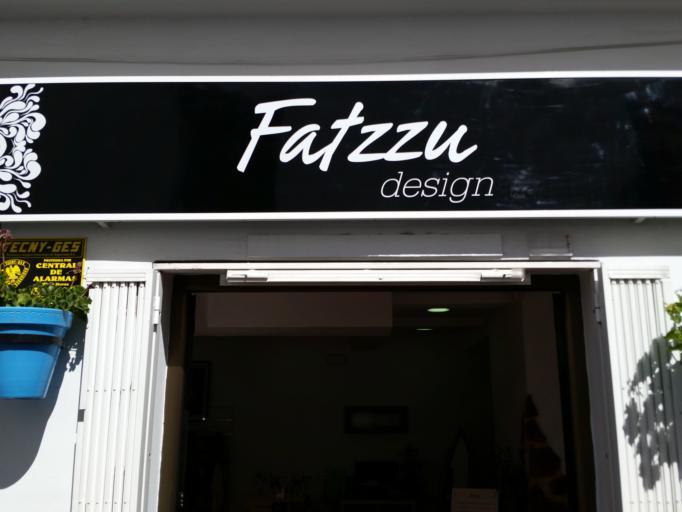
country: ES
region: Andalusia
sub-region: Provincia de Malaga
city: Mijas
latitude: 36.5966
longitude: -4.6379
